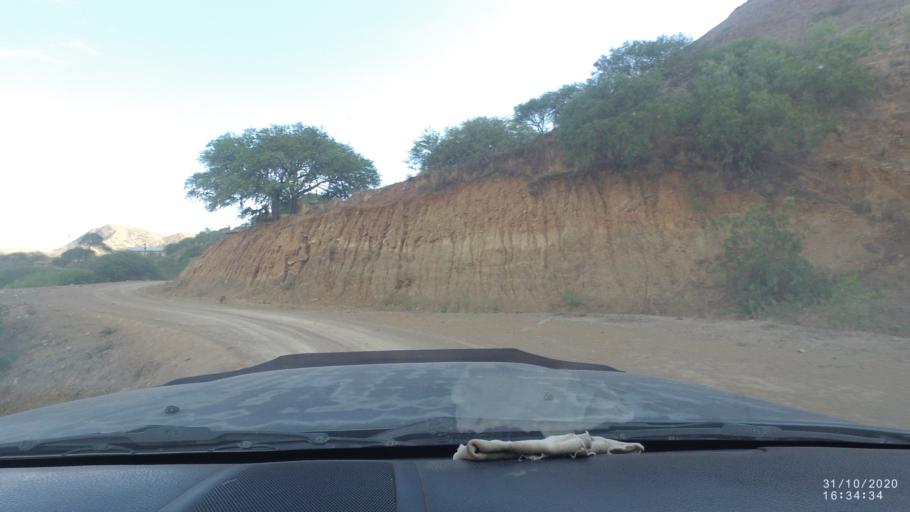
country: BO
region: Chuquisaca
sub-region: Provincia Zudanez
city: Mojocoya
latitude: -18.4491
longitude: -64.5842
